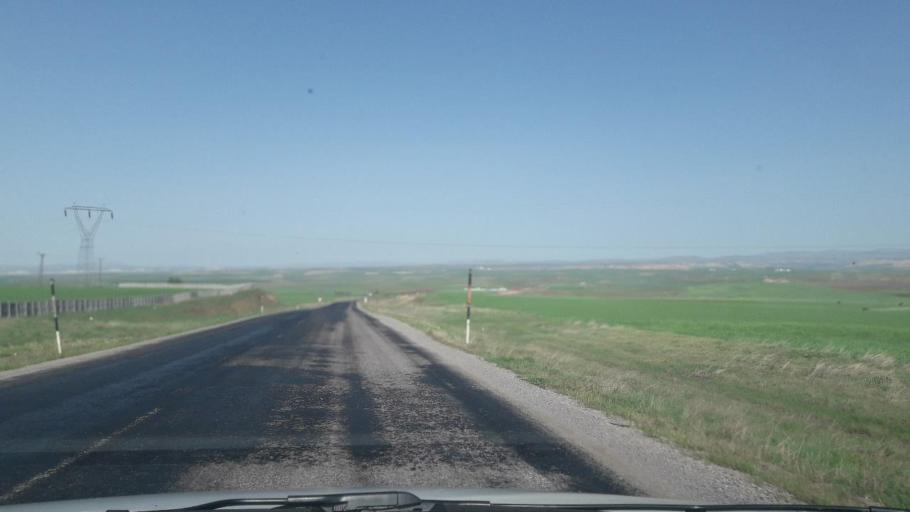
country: TR
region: Sivas
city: Kangal
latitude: 39.1712
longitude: 37.4629
